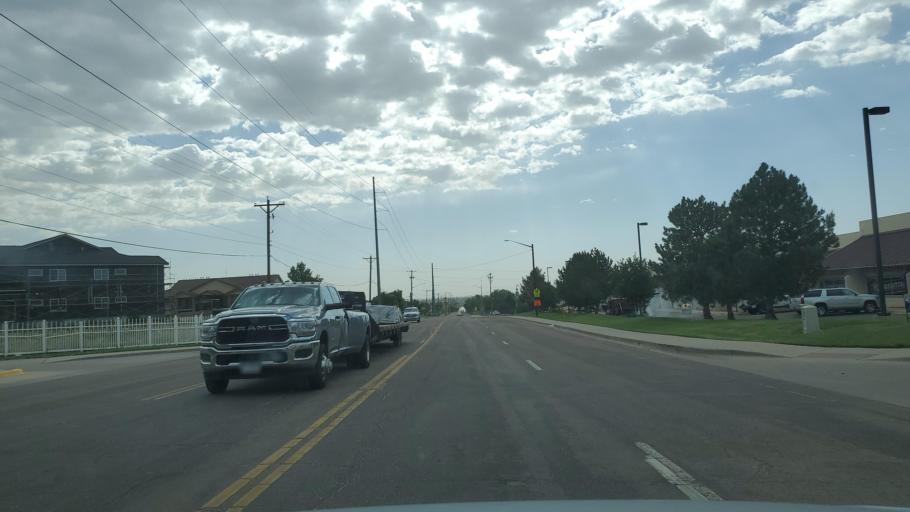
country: US
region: Colorado
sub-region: Adams County
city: Welby
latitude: 39.8381
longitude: -104.9771
